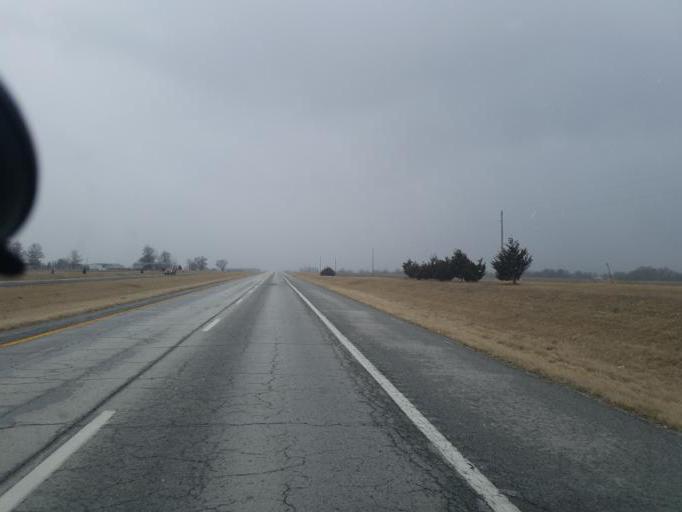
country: US
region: Missouri
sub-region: Macon County
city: La Plata
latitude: 40.0112
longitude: -92.4752
